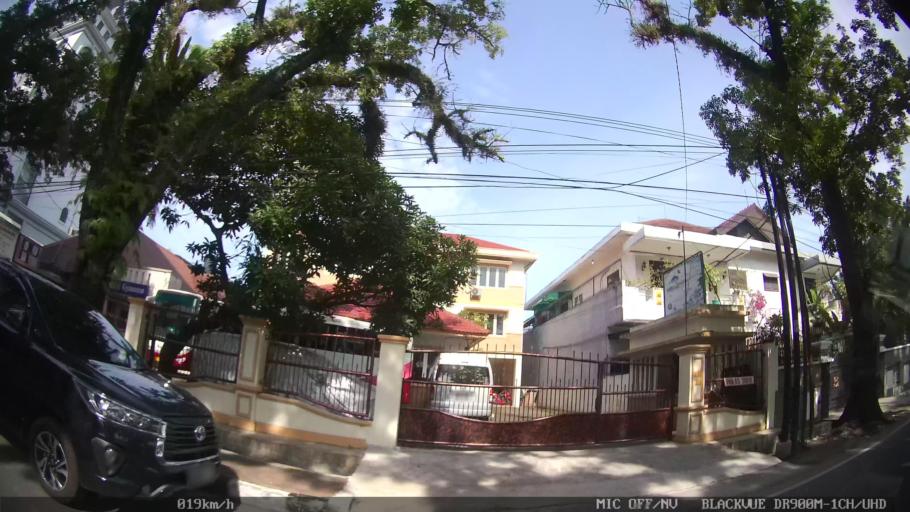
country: ID
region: North Sumatra
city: Medan
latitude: 3.5775
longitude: 98.6574
